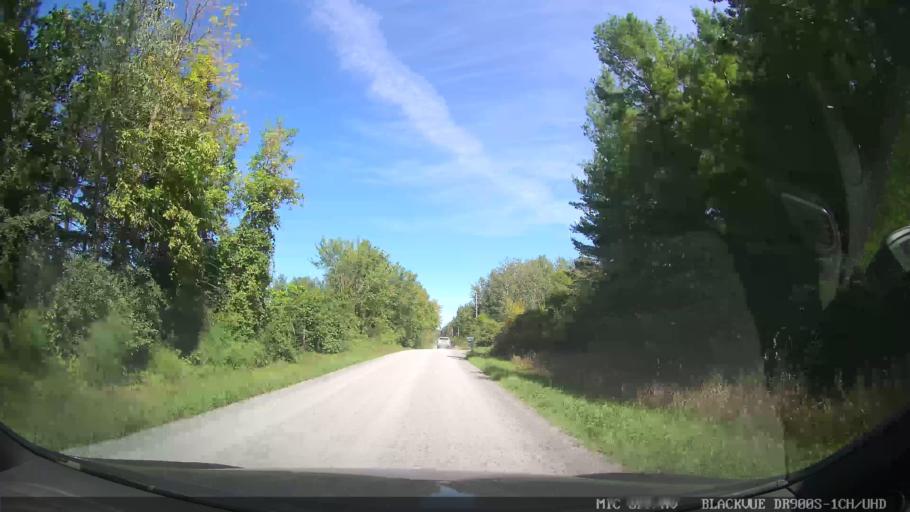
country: CA
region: Ontario
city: Bells Corners
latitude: 45.0819
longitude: -75.7083
